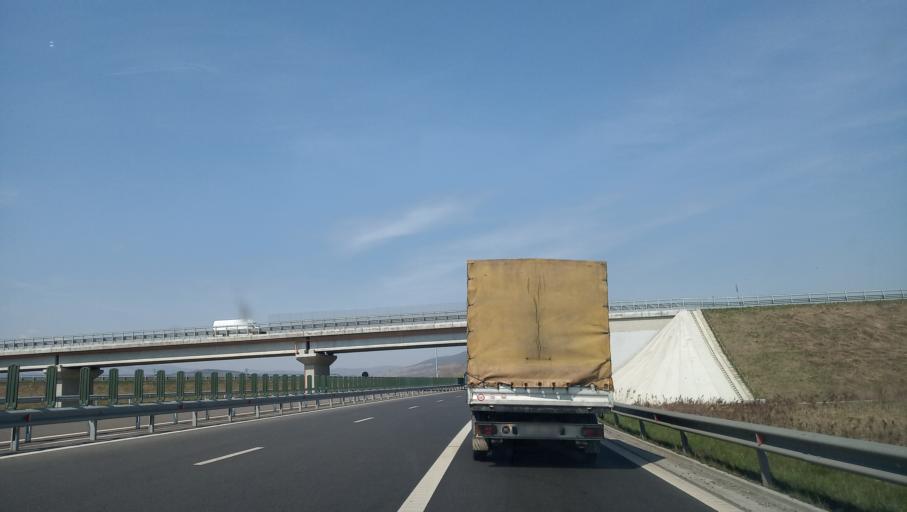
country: RO
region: Alba
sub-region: Municipiul Aiud
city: Aiud
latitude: 46.3287
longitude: 23.7295
